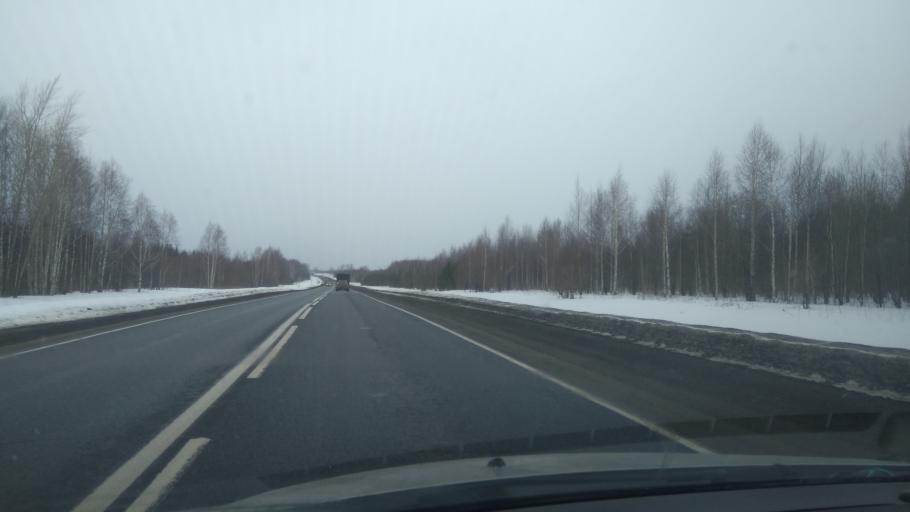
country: RU
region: Perm
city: Orda
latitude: 57.2281
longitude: 57.0729
